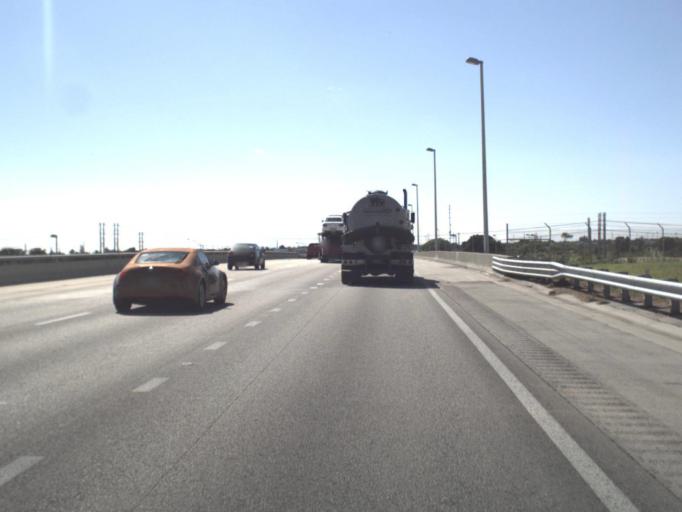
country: US
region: Florida
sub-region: Miami-Dade County
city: Three Lakes
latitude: 25.6495
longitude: -80.3867
